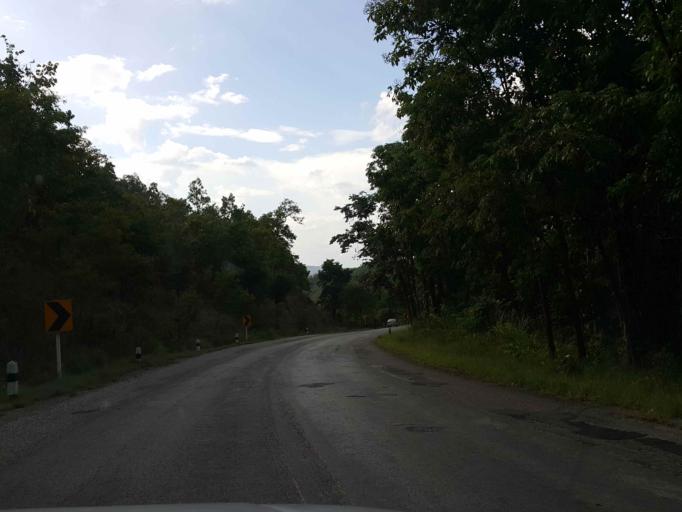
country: TH
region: Lampang
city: Thoen
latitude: 17.6274
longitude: 99.3122
